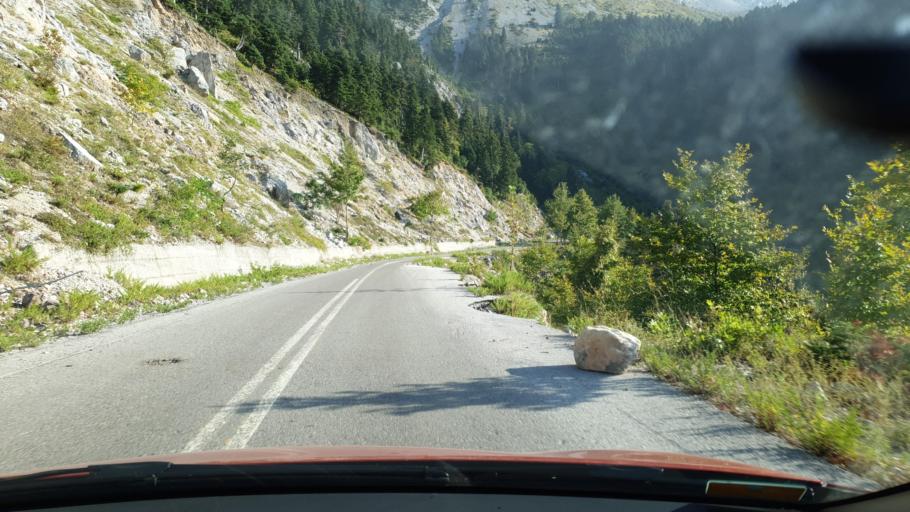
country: GR
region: Central Greece
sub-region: Nomos Evvoias
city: Yimnon
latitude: 38.5965
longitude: 23.9064
